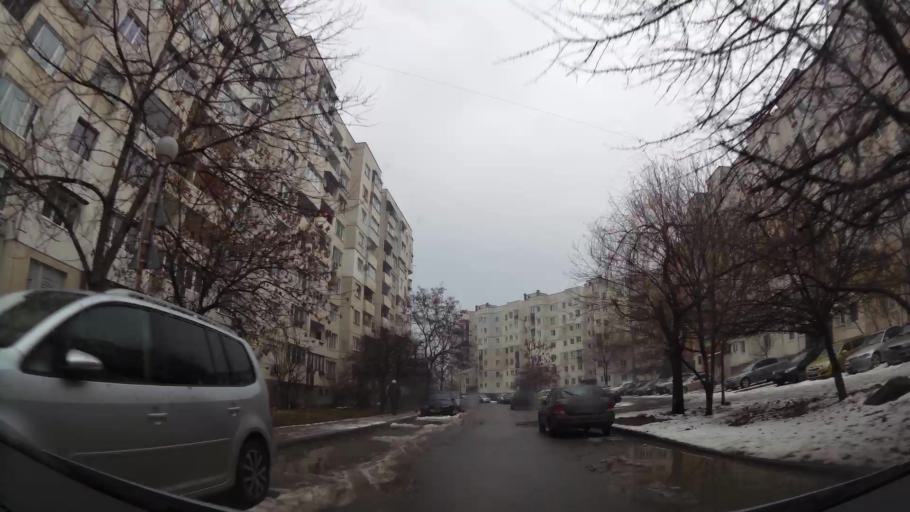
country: BG
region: Sofia-Capital
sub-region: Stolichna Obshtina
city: Sofia
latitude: 42.6865
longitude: 23.2582
